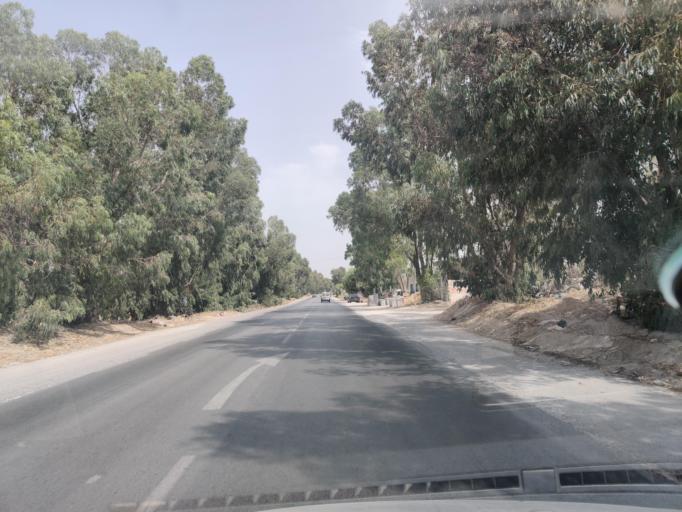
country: TN
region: Nabul
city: Al Hammamat
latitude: 36.4491
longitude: 10.5722
